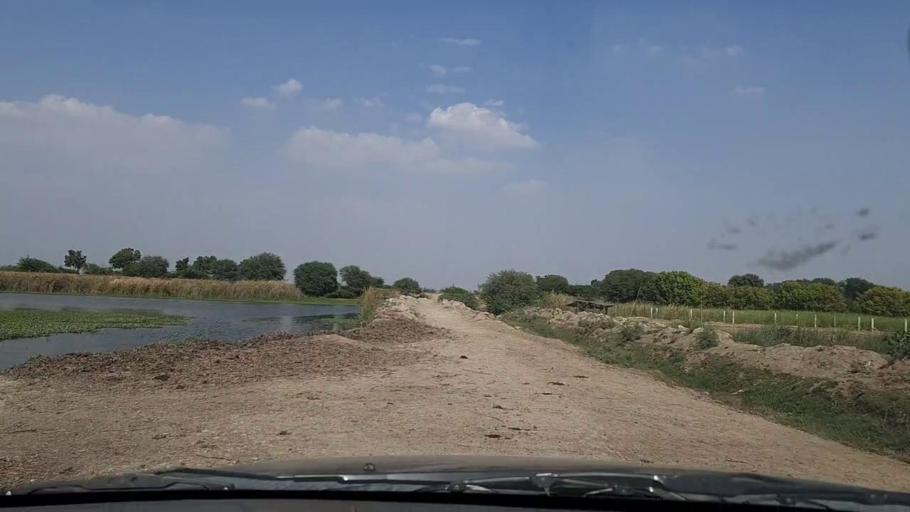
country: PK
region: Sindh
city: Mirpur Batoro
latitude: 24.6249
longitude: 68.2426
